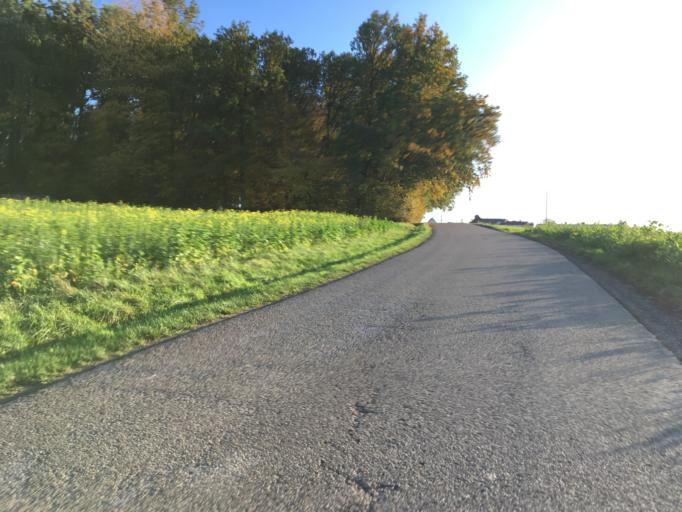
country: DE
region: Baden-Wuerttemberg
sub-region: Regierungsbezirk Stuttgart
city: Neuenstein
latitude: 49.2326
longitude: 9.6117
